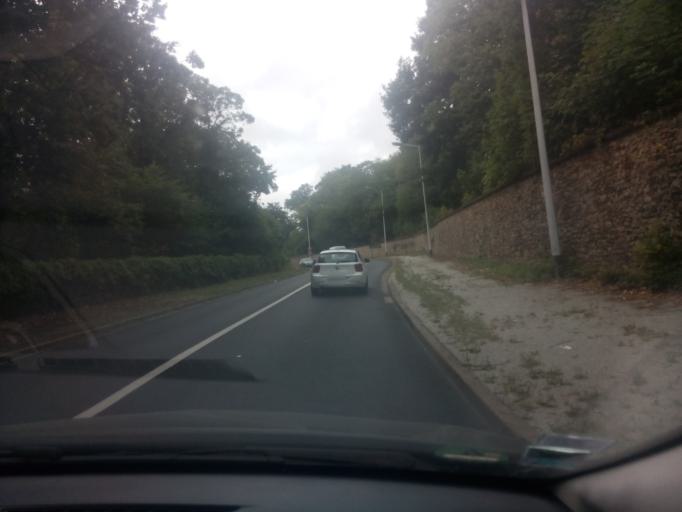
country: FR
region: Ile-de-France
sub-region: Departement des Yvelines
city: Jouy-en-Josas
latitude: 48.7585
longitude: 2.1752
